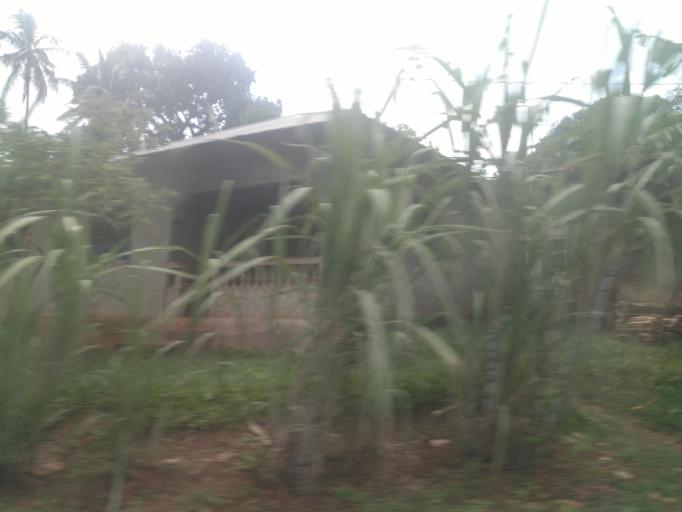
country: TZ
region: Zanzibar Urban/West
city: Zanzibar
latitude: -6.2700
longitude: 39.2675
